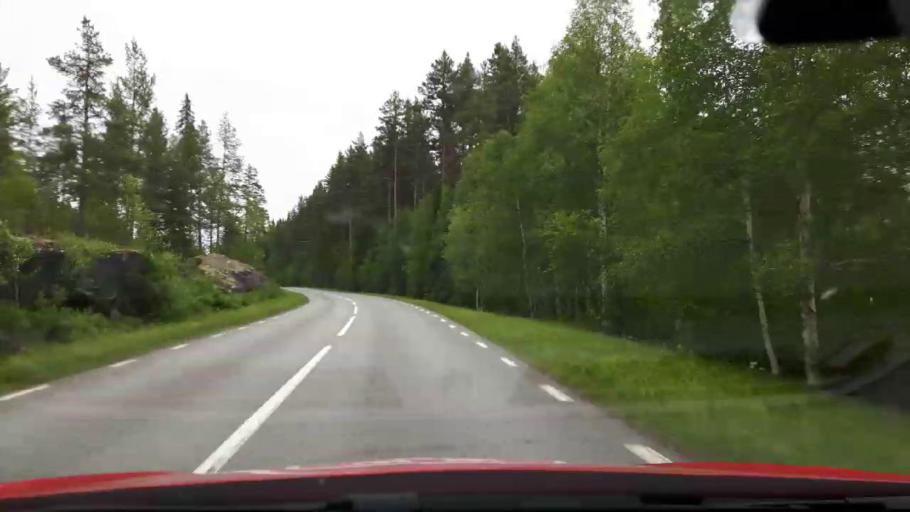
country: SE
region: Jaemtland
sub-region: Stroemsunds Kommun
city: Stroemsund
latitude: 63.4283
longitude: 15.5047
